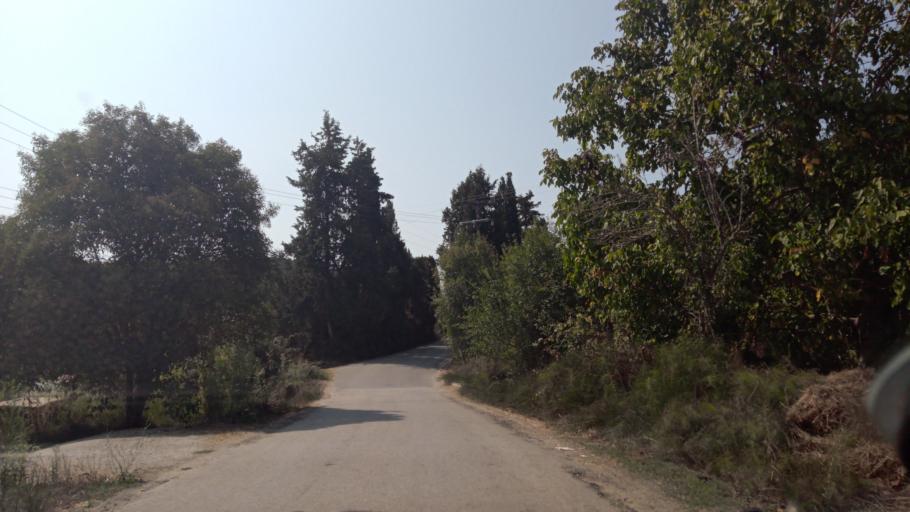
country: GR
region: Ionian Islands
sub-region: Nomos Kerkyras
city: Perivoli
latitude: 39.4026
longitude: 20.0265
